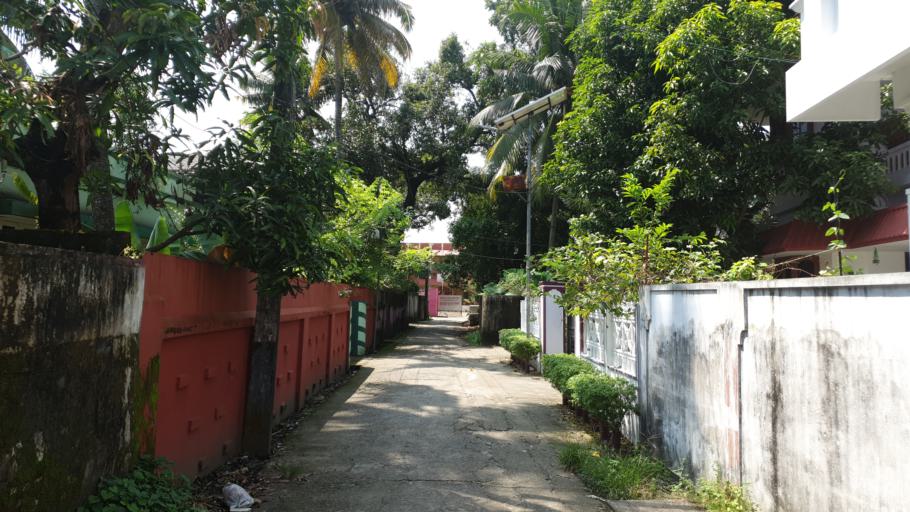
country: IN
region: Kerala
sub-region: Ernakulam
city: Cochin
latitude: 9.9754
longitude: 76.2420
